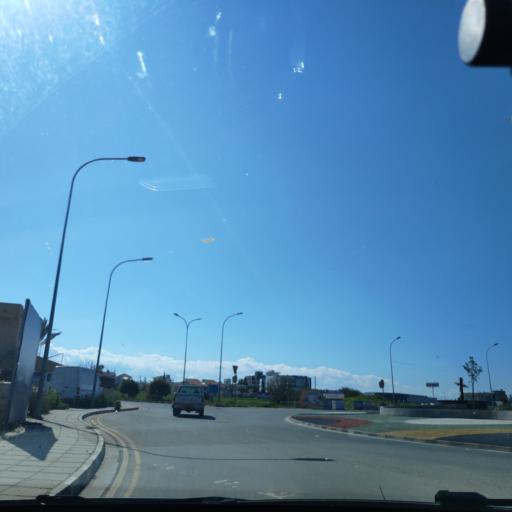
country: CY
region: Lefkosia
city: Tseri
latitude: 35.1118
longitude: 33.3130
